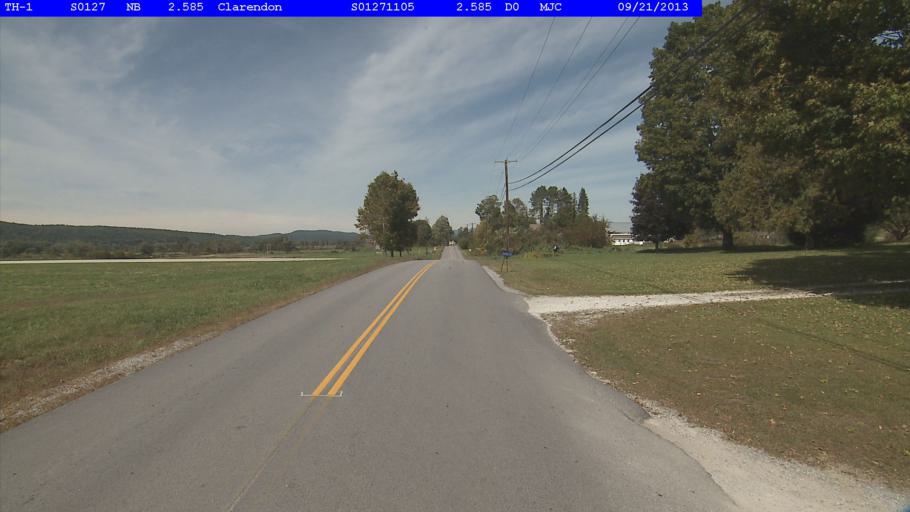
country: US
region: Vermont
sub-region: Rutland County
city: Rutland
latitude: 43.5507
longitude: -72.9703
